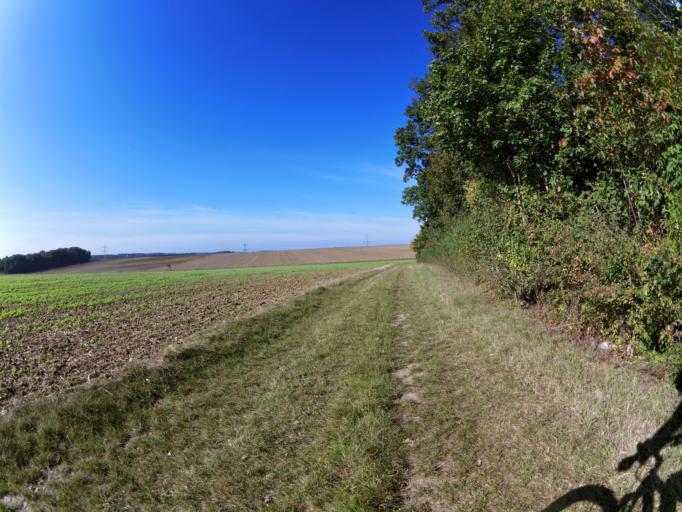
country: DE
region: Bavaria
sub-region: Regierungsbezirk Unterfranken
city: Ochsenfurt
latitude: 49.6784
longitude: 10.0635
